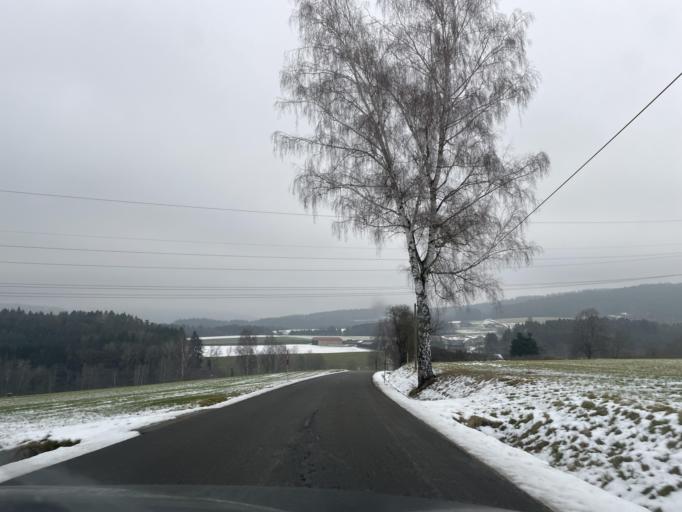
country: DE
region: Bavaria
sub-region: Lower Bavaria
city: Geiersthal
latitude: 49.0408
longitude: 12.9273
